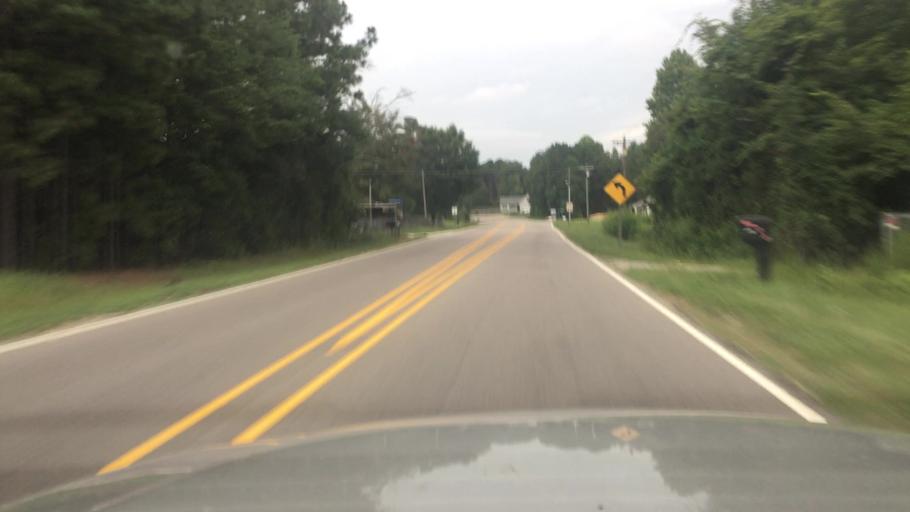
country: US
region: North Carolina
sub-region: Hoke County
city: Rockfish
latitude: 34.9652
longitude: -79.0528
